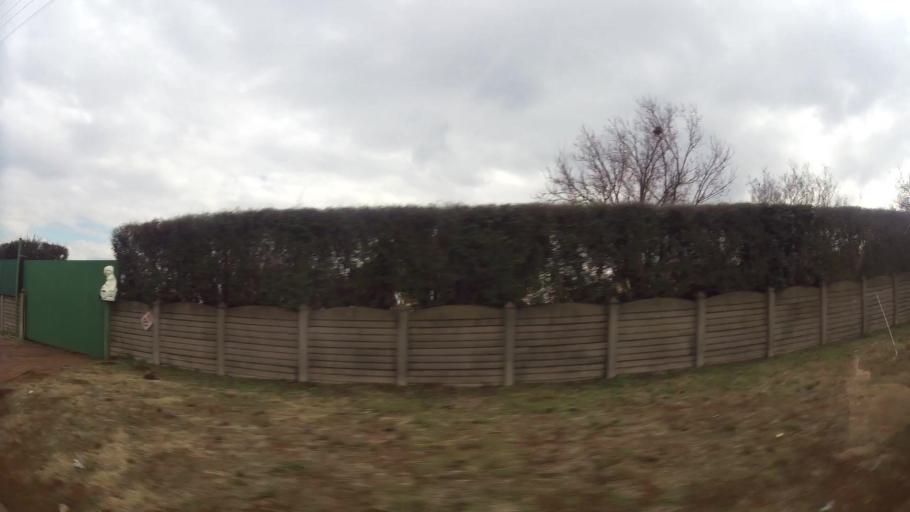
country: ZA
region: Gauteng
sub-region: Sedibeng District Municipality
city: Meyerton
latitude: -26.5866
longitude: 28.0003
